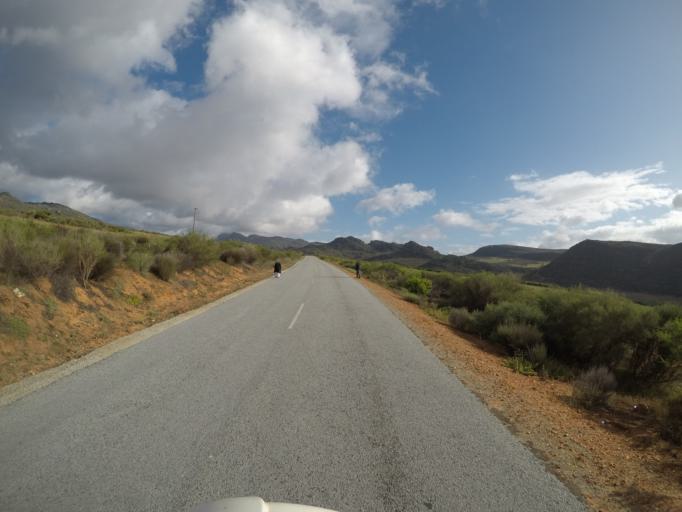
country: ZA
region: Western Cape
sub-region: West Coast District Municipality
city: Clanwilliam
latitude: -32.4295
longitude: 18.9382
